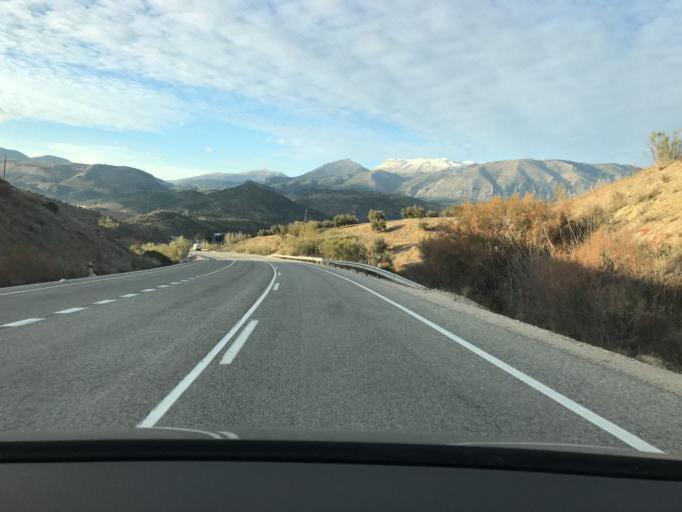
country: ES
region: Andalusia
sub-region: Provincia de Jaen
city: Huelma
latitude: 37.6389
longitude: -3.4117
